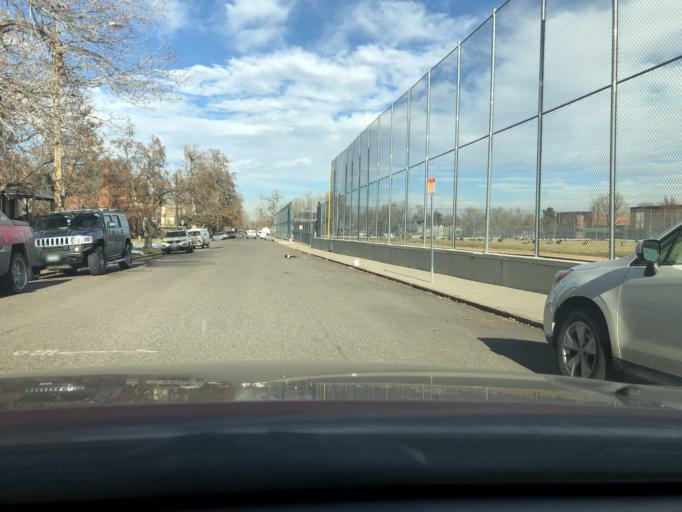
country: US
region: Colorado
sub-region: Denver County
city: Denver
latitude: 39.7550
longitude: -104.9697
